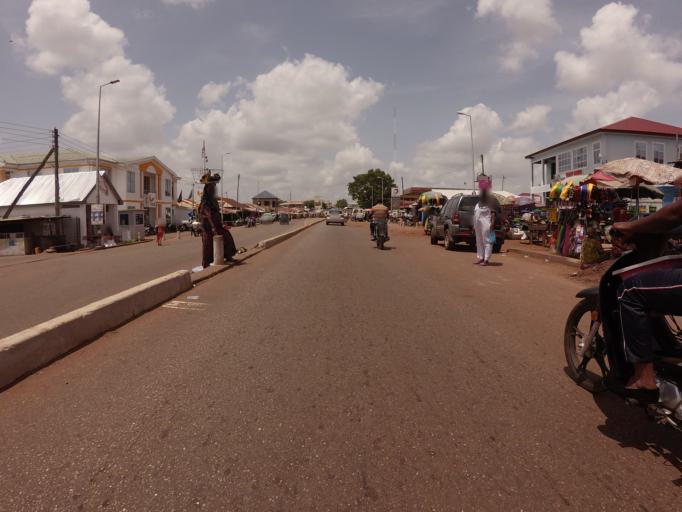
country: GH
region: Northern
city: Tamale
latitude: 9.4043
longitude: -0.8475
